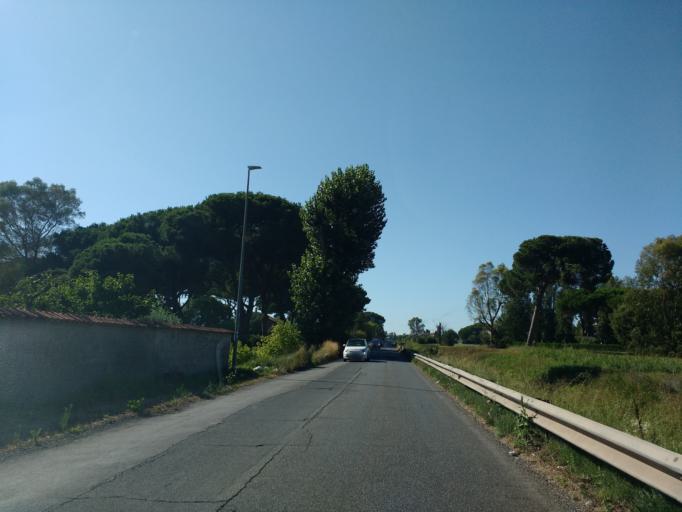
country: IT
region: Latium
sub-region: Citta metropolitana di Roma Capitale
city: Acilia-Castel Fusano-Ostia Antica
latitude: 41.7419
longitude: 12.3396
